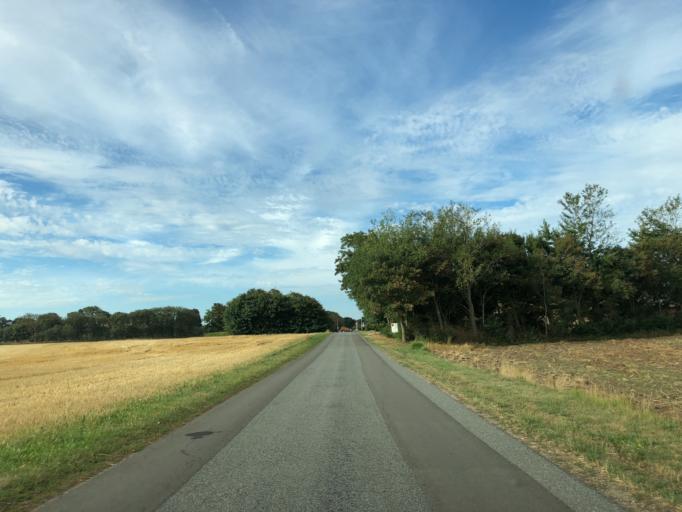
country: DK
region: Central Jutland
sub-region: Ringkobing-Skjern Kommune
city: Skjern
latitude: 56.0570
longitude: 8.4088
